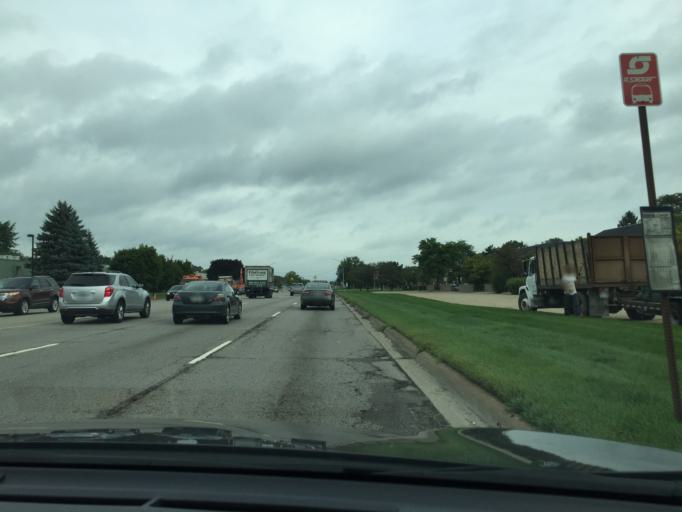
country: US
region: Michigan
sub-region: Oakland County
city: Southfield
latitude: 42.4778
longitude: -83.2213
